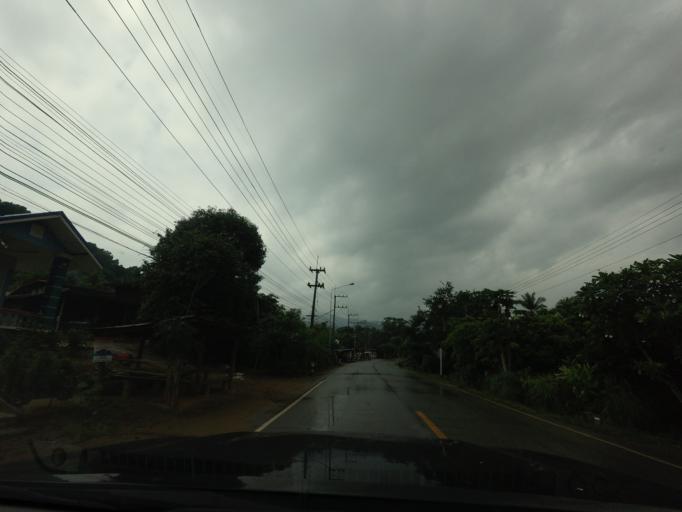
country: TH
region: Nong Khai
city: Sangkhom
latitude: 18.1063
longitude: 102.2295
